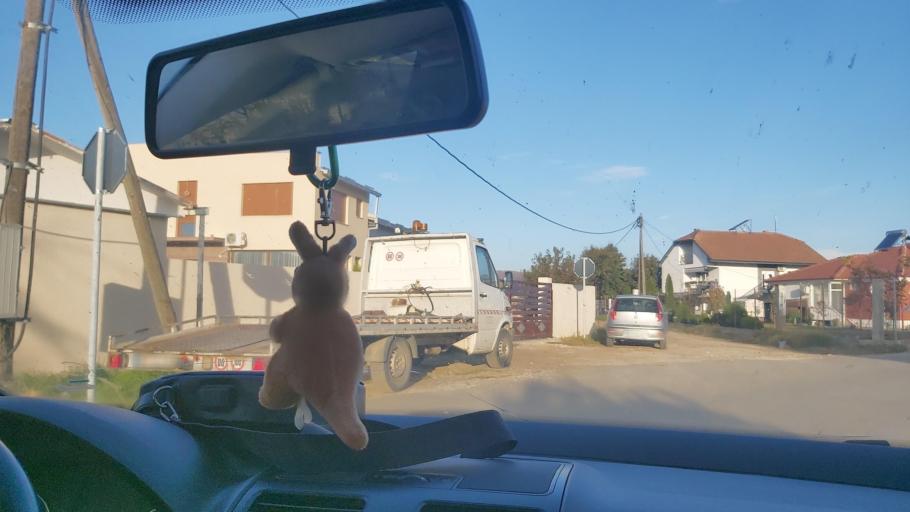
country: MK
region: Vasilevo
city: Vasilevo
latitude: 41.4675
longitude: 22.6429
